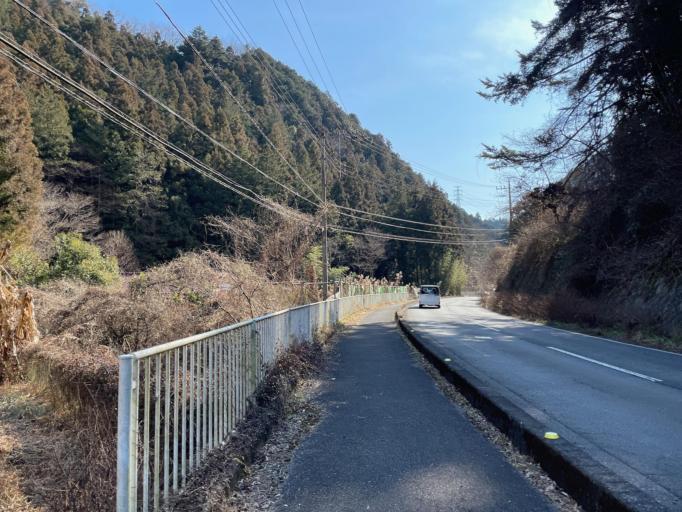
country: JP
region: Saitama
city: Hanno
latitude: 35.8489
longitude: 139.2555
